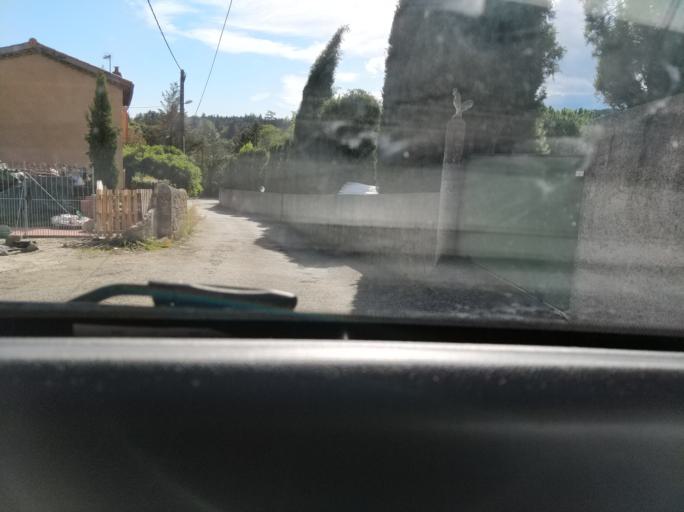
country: FR
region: Rhone-Alpes
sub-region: Departement de l'Ardeche
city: Boulieu-les-Annonay
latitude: 45.2686
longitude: 4.6649
